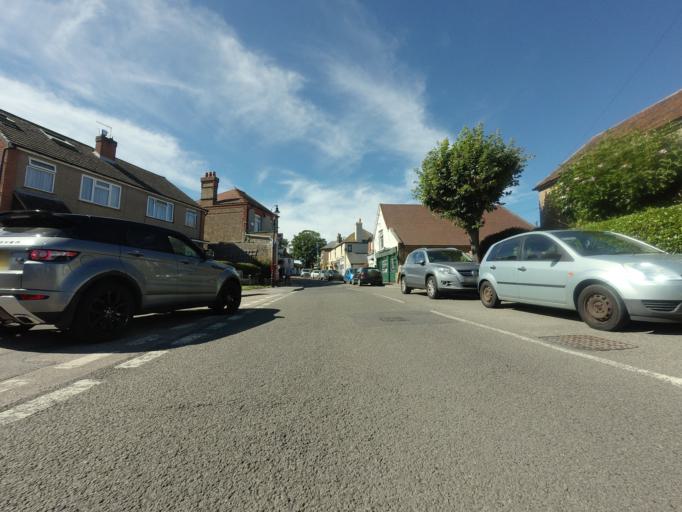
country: GB
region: England
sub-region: Kent
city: Birchington-on-Sea
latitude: 51.3340
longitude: 1.3150
